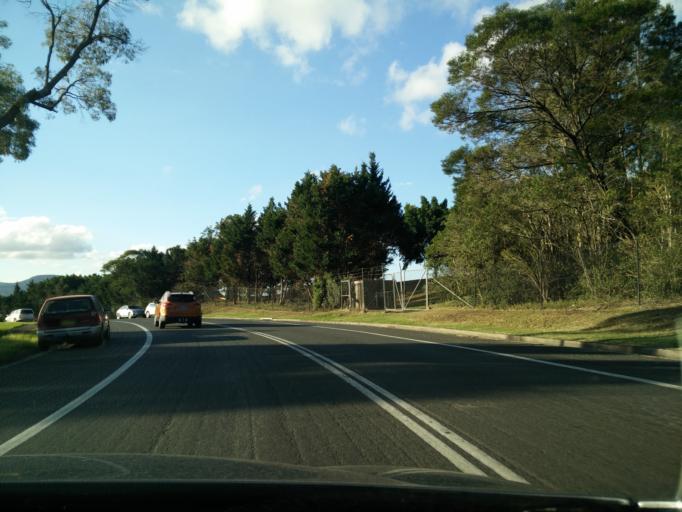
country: AU
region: New South Wales
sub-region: Wollongong
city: Berkeley
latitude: -34.4679
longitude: 150.8462
